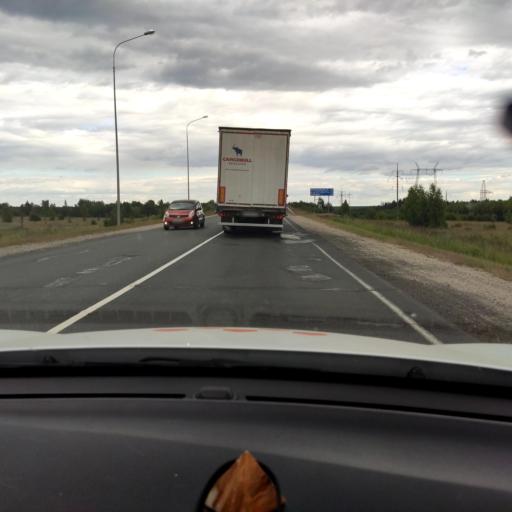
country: RU
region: Mariy-El
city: Volzhsk
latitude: 55.9110
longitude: 48.3696
